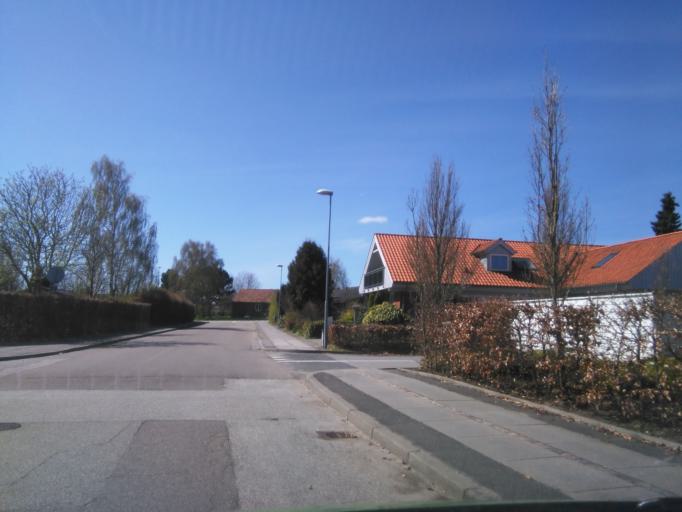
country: DK
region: Central Jutland
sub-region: Arhus Kommune
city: Solbjerg
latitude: 56.0440
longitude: 10.0839
